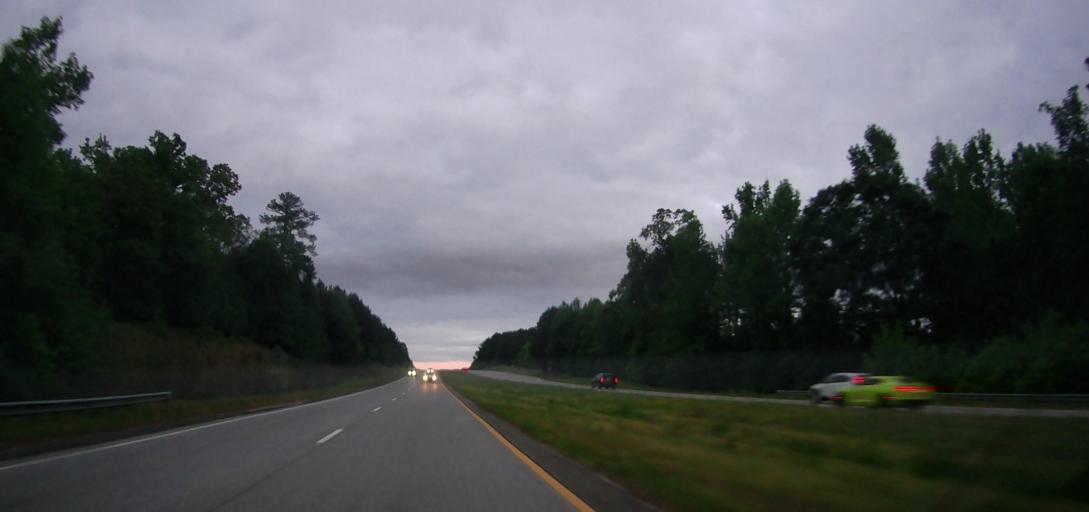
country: US
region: Georgia
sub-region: Jackson County
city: Jefferson
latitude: 34.1111
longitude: -83.5975
